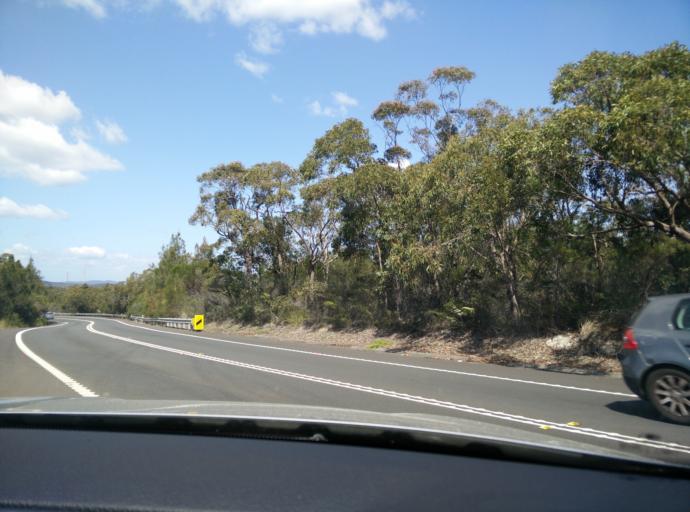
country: AU
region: New South Wales
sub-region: Gosford Shire
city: Blackwall
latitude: -33.4718
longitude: 151.2880
